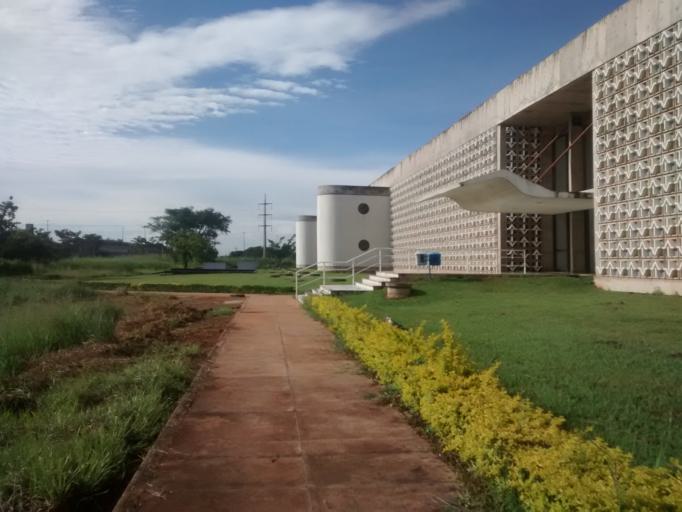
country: BR
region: Federal District
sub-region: Brasilia
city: Brasilia
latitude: -15.7679
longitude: -47.8649
